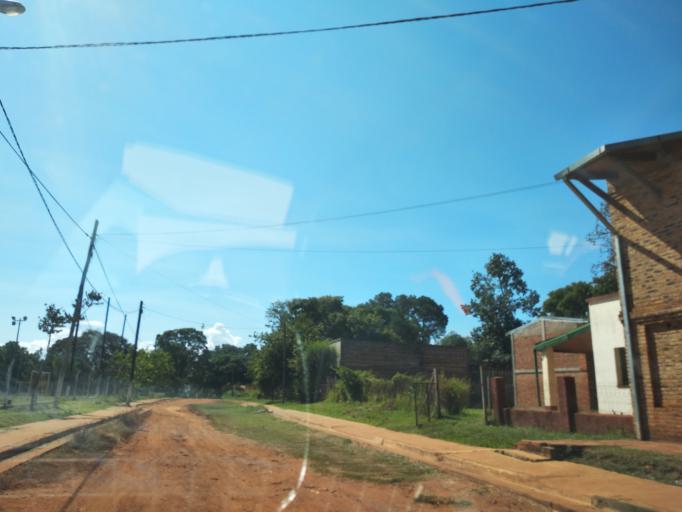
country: AR
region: Misiones
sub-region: Departamento de Capital
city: Posadas
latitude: -27.4299
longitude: -55.8838
